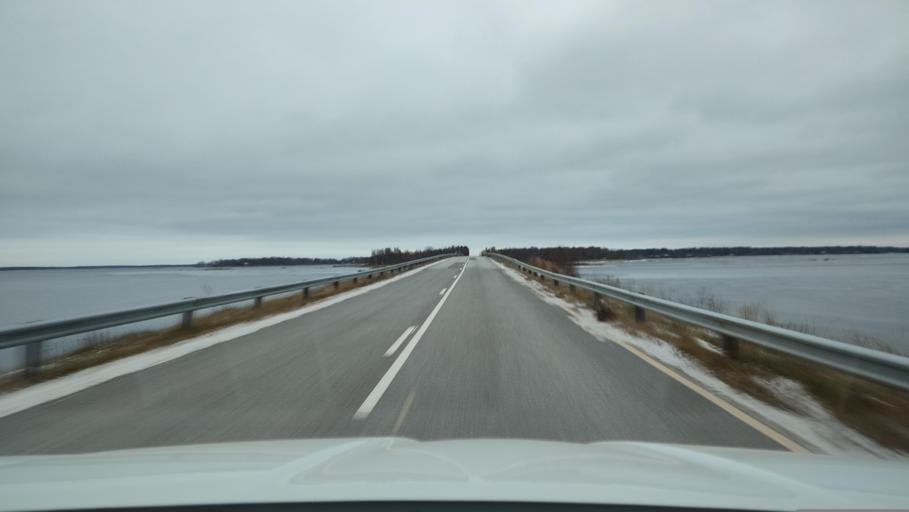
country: FI
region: Ostrobothnia
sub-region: Vaasa
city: Replot
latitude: 63.2724
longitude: 21.3447
